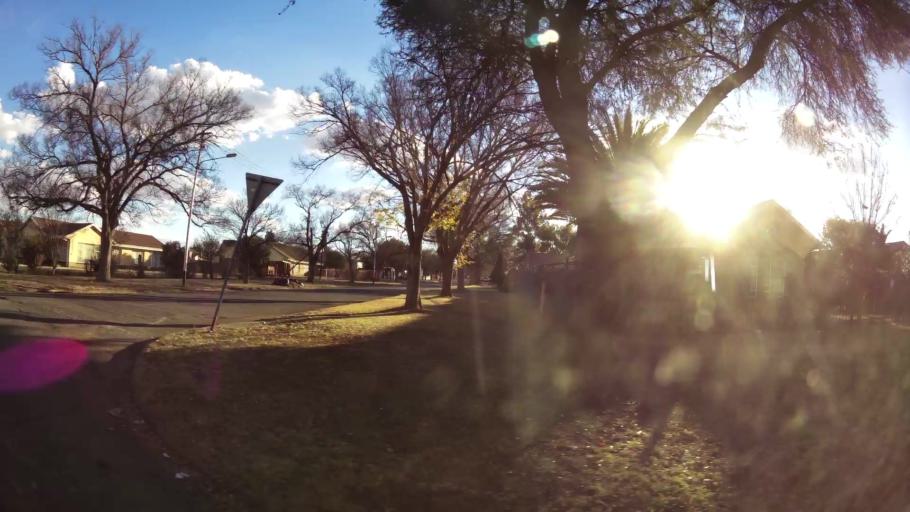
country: ZA
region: North-West
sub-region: Dr Kenneth Kaunda District Municipality
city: Potchefstroom
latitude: -26.7317
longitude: 27.0894
